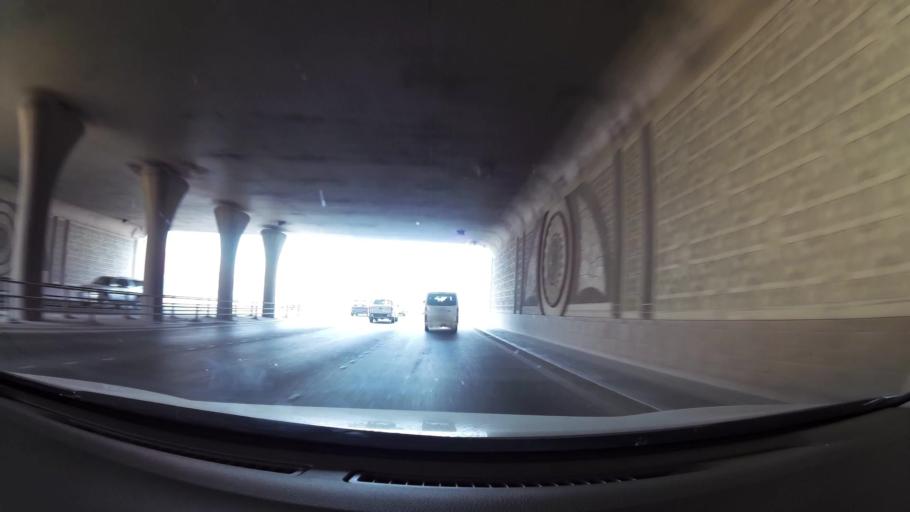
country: QA
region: Baladiyat ad Dawhah
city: Doha
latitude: 25.2594
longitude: 51.5000
